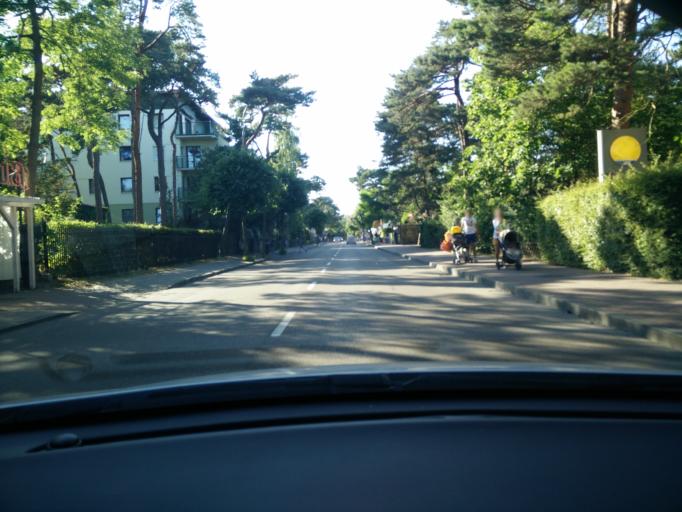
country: PL
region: Pomeranian Voivodeship
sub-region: Powiat pucki
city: Jastarnia
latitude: 54.6823
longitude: 18.7160
